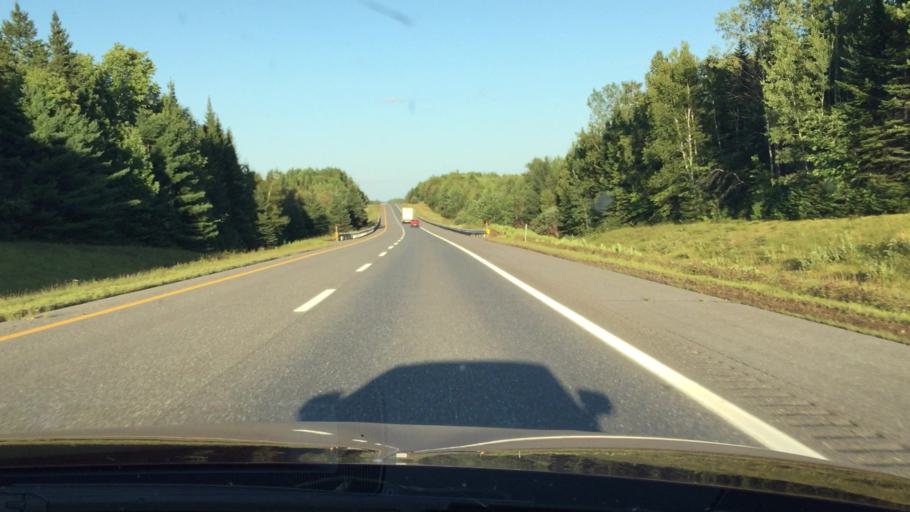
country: US
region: Maine
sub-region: Aroostook County
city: Hodgdon
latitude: 46.1399
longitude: -68.0141
